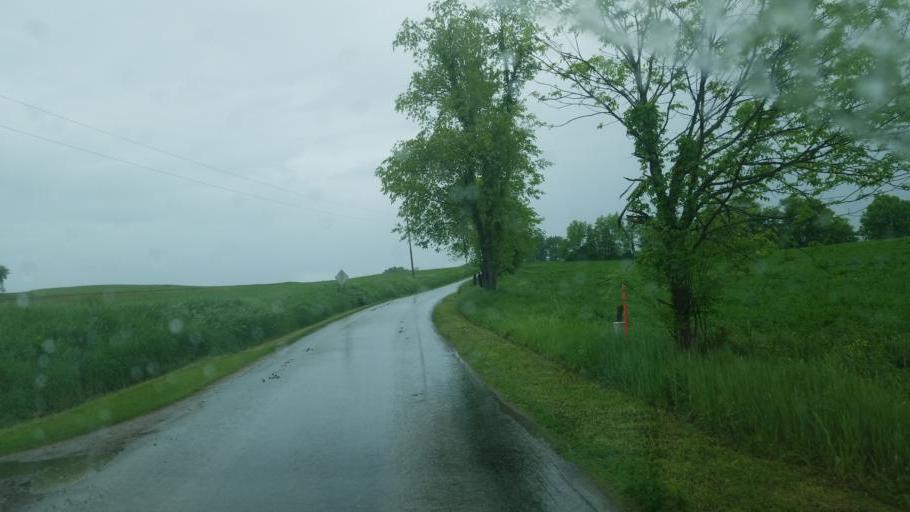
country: US
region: Ohio
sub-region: Wayne County
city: Apple Creek
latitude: 40.7280
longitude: -81.8632
